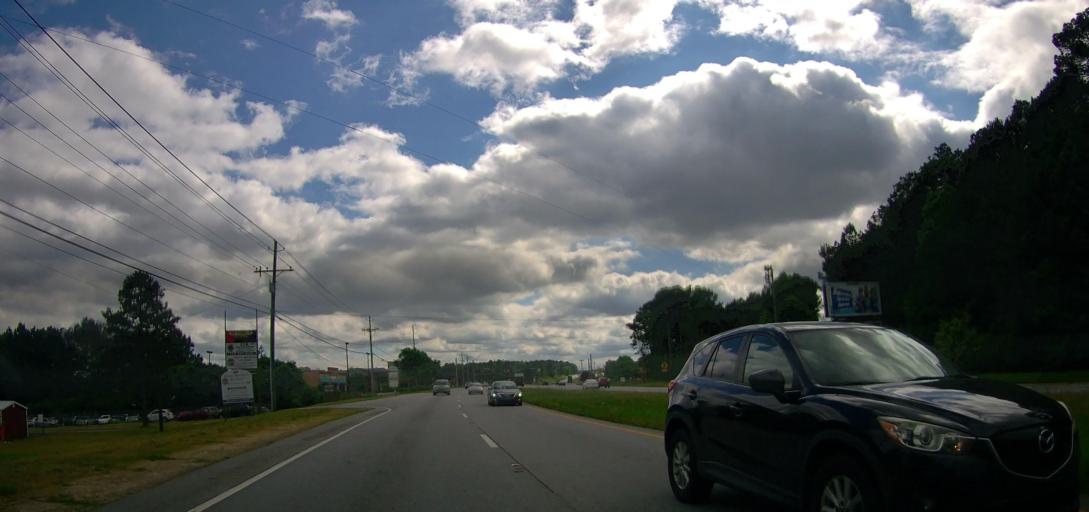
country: US
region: Georgia
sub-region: Rockdale County
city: Conyers
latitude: 33.6739
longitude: -83.9799
